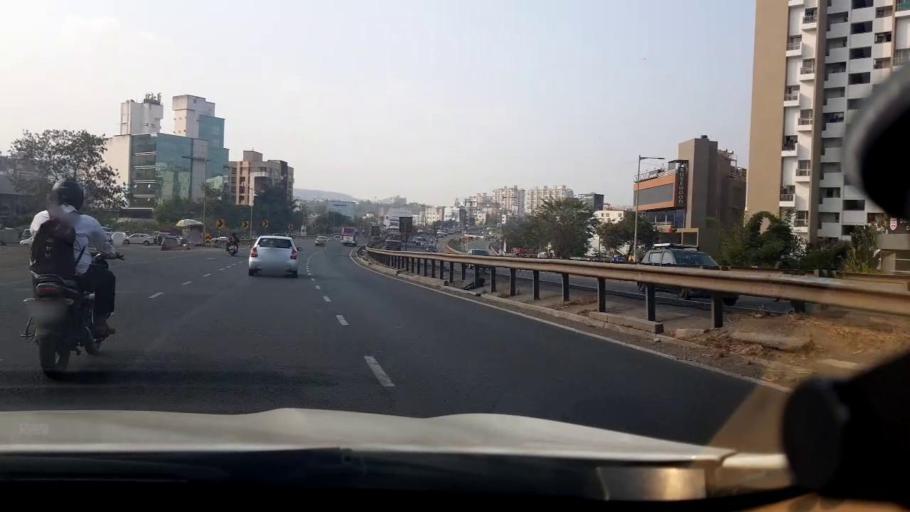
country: IN
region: Maharashtra
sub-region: Pune Division
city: Kharakvasla
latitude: 18.5112
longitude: 73.7718
